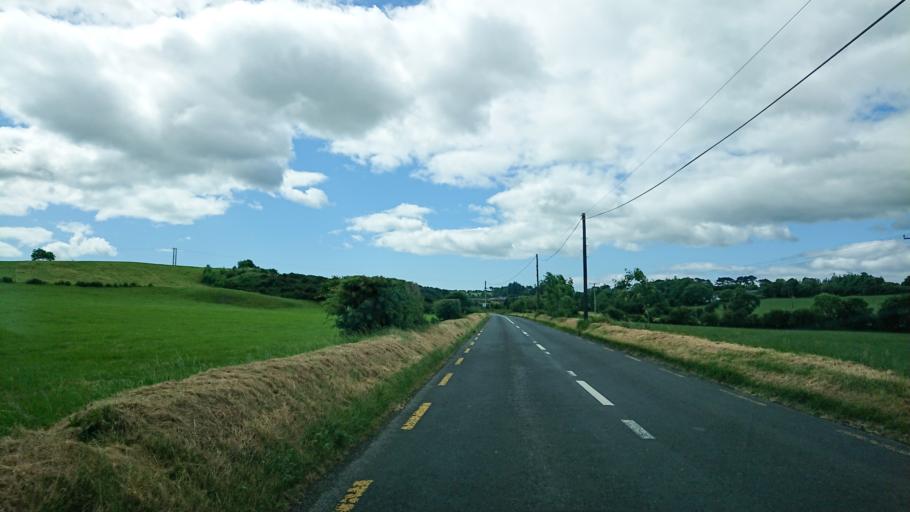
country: IE
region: Leinster
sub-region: Kilkenny
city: Mooncoin
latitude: 52.2269
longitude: -7.2000
